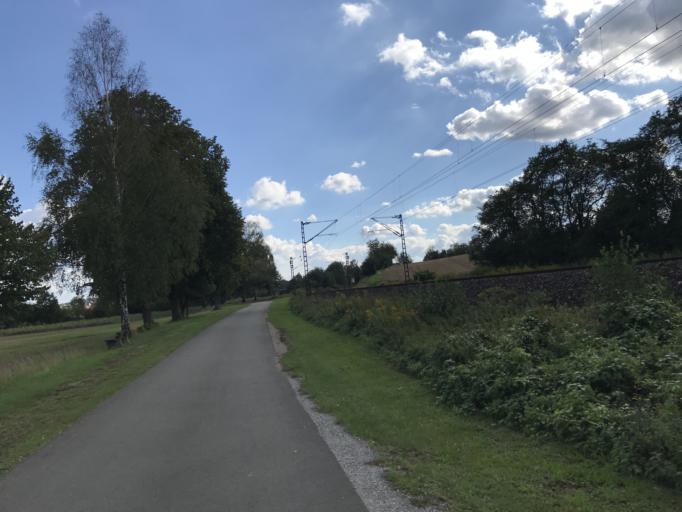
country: DE
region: Hesse
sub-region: Regierungsbezirk Kassel
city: Eschwege
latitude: 51.2083
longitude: 10.0004
